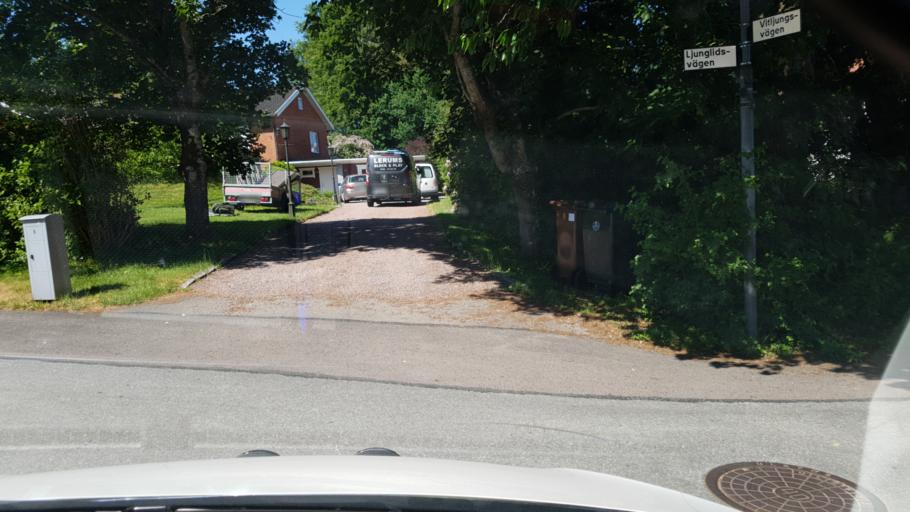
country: SE
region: Vaestra Goetaland
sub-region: Lerums Kommun
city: Stenkullen
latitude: 57.8047
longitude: 12.3609
